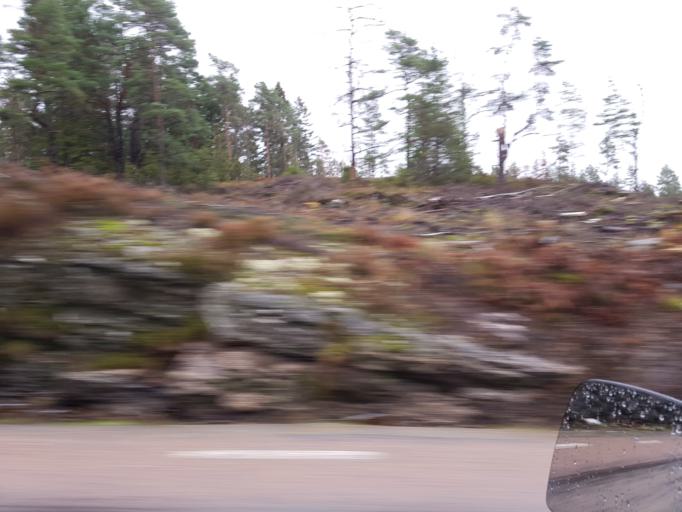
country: SE
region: Vaestra Goetaland
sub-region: Orust
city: Henan
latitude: 58.2718
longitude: 11.7208
